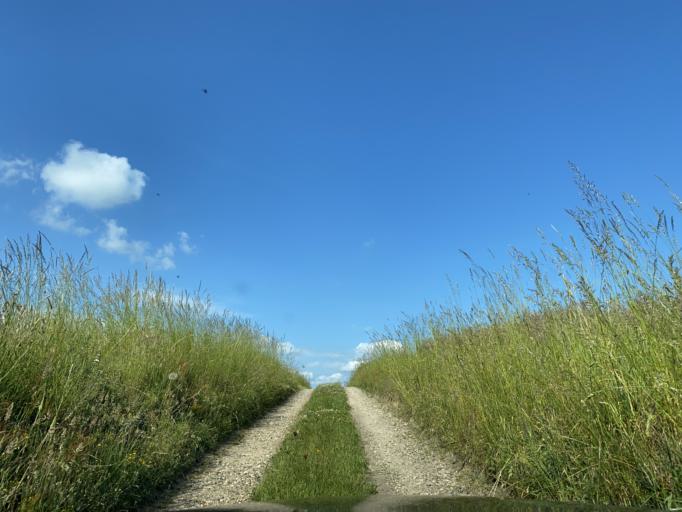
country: DK
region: Central Jutland
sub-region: Silkeborg Kommune
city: Svejbaek
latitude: 56.2417
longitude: 9.6946
